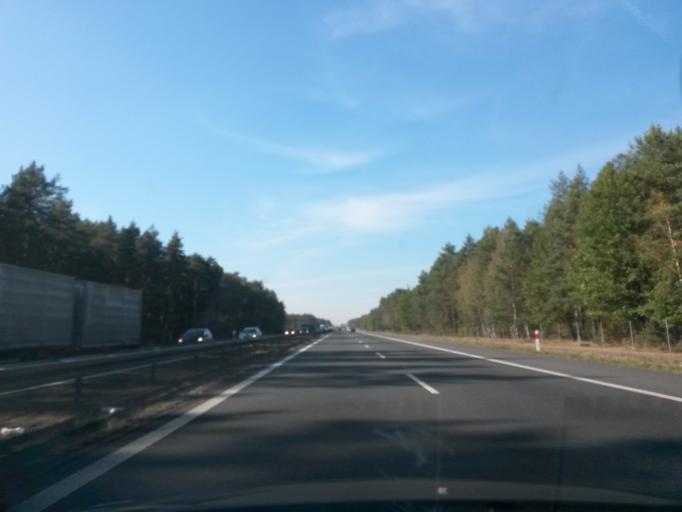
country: PL
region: Opole Voivodeship
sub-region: Powiat opolski
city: Komprachcice
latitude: 50.6110
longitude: 17.7768
